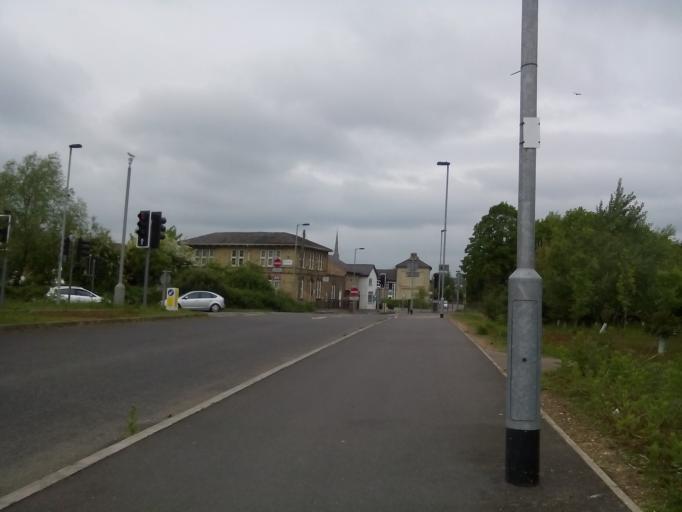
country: GB
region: England
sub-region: Cambridgeshire
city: Hemingford Grey
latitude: 52.3212
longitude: -0.0675
